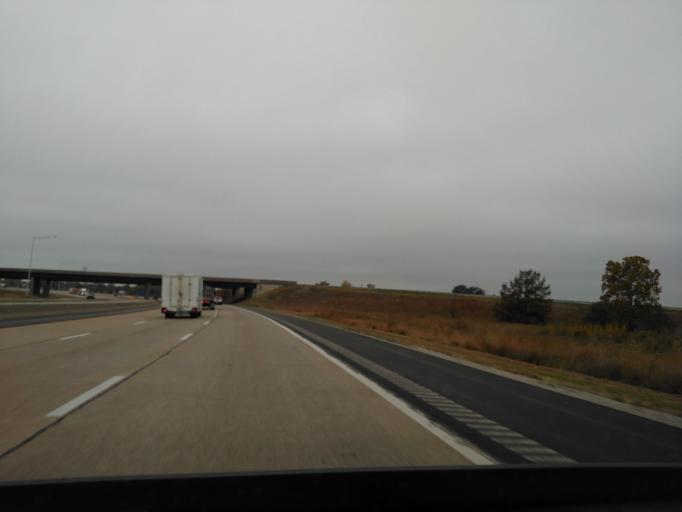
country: US
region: Illinois
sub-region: Saint Clair County
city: Dupo
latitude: 38.5317
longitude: -90.1949
